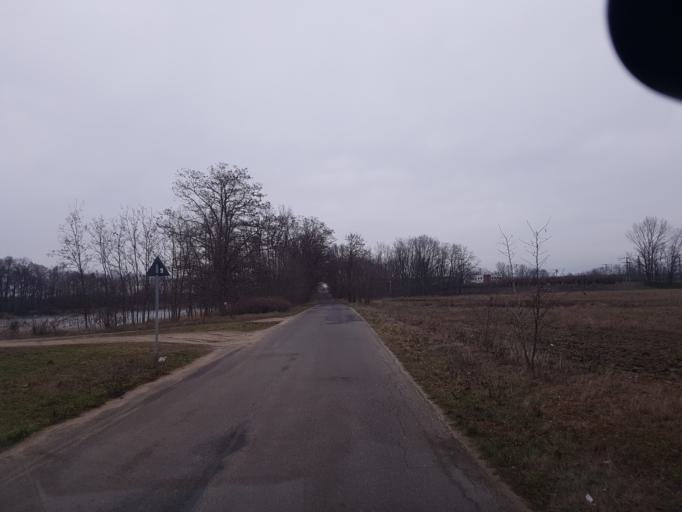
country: DE
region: Brandenburg
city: Falkenberg
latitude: 51.5789
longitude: 13.2546
